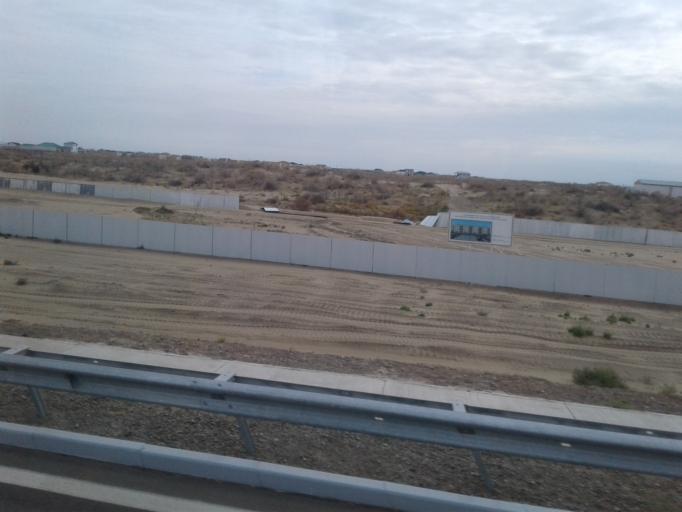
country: TM
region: Lebap
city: Turkmenabat
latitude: 38.9740
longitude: 63.5468
